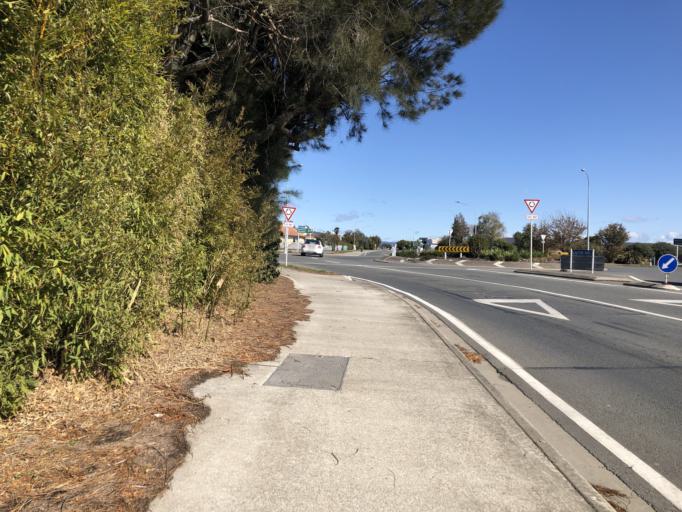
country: NZ
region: Tasman
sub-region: Tasman District
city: Richmond
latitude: -41.3452
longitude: 173.1683
